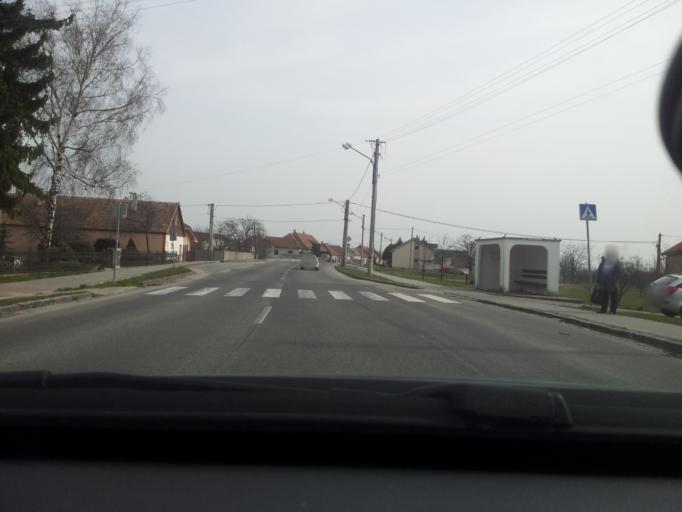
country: SK
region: Trnavsky
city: Leopoldov
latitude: 48.4395
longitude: 17.7147
